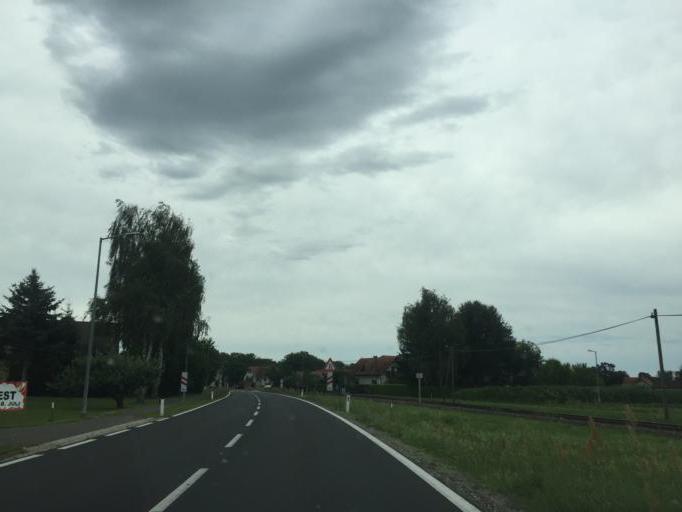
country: SI
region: Apace
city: Apace
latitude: 46.7316
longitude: 15.9047
